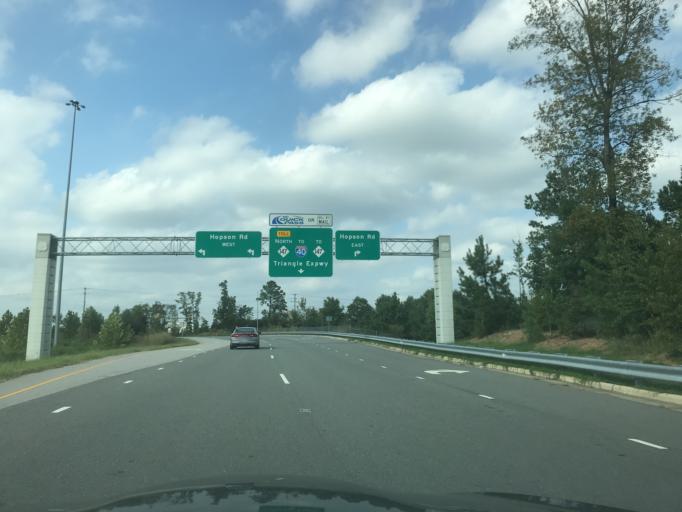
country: US
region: North Carolina
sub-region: Wake County
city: Morrisville
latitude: 35.8751
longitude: -78.8655
